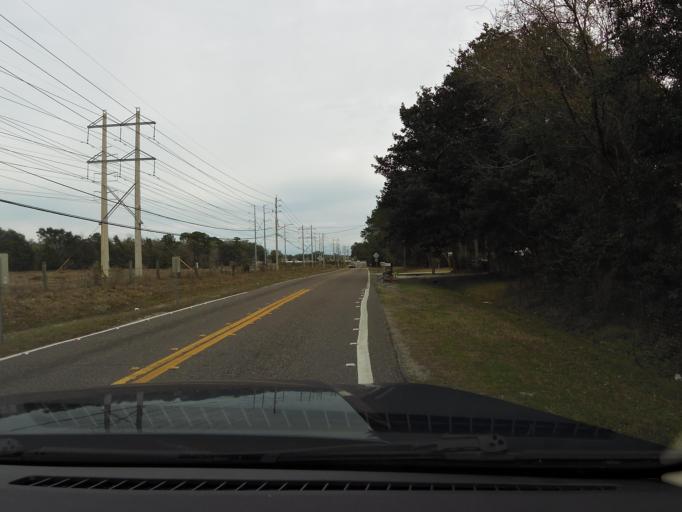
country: US
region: Florida
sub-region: Duval County
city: Jacksonville
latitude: 30.4547
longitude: -81.6014
